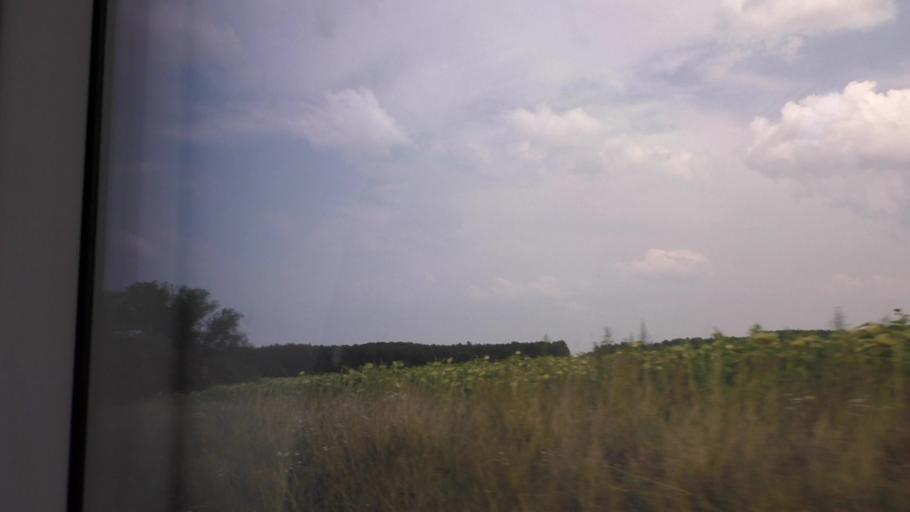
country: DE
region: Brandenburg
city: Mixdorf
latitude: 52.1913
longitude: 14.3904
